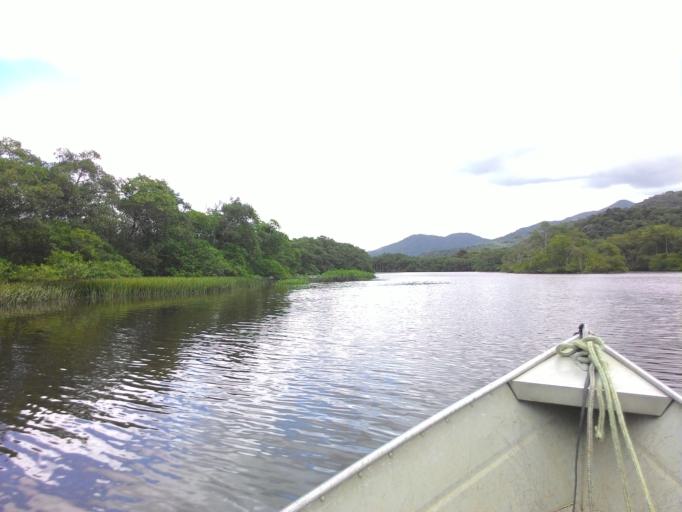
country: BR
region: Sao Paulo
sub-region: Pariquera-Acu
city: Pariquera Acu
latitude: -24.8694
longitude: -47.7992
